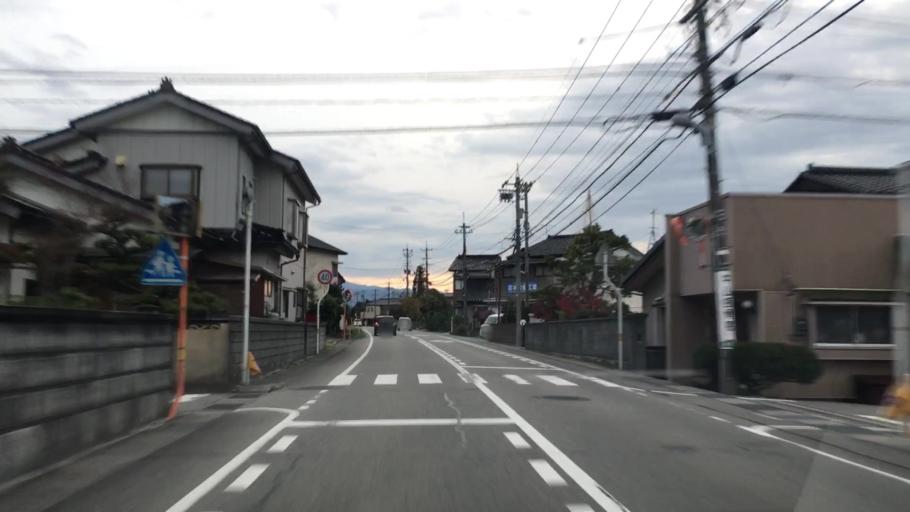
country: JP
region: Toyama
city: Kamiichi
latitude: 36.6984
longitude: 137.3151
